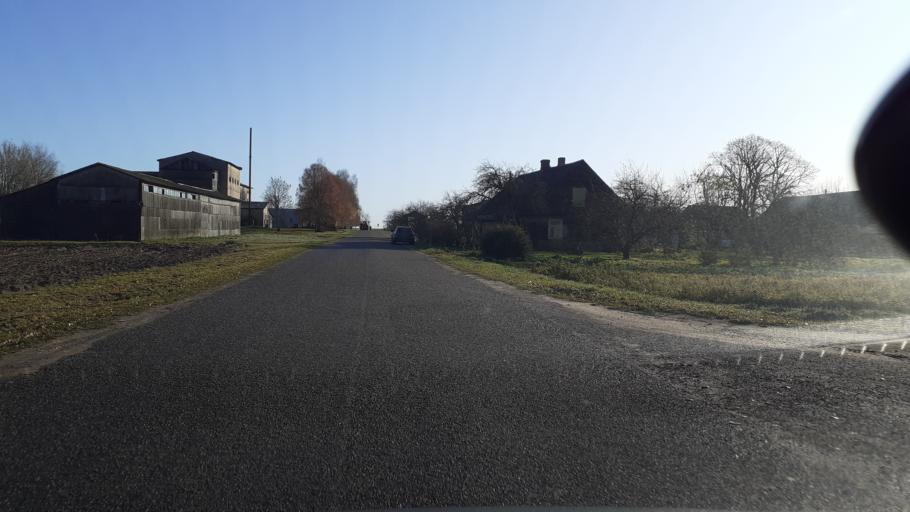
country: LV
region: Kuldigas Rajons
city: Kuldiga
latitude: 56.9974
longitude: 21.8945
